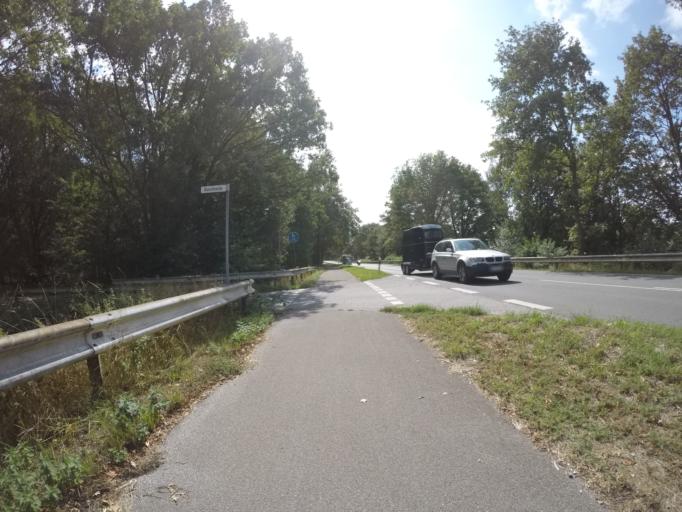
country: DE
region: North Rhine-Westphalia
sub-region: Regierungsbezirk Munster
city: Isselburg
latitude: 51.8036
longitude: 6.4767
